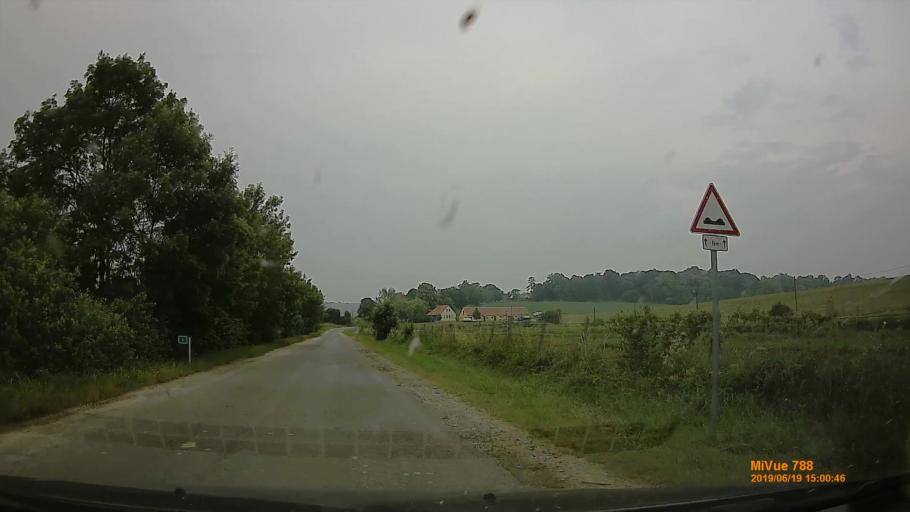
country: HU
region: Baranya
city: Szigetvar
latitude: 46.0833
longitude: 17.8044
